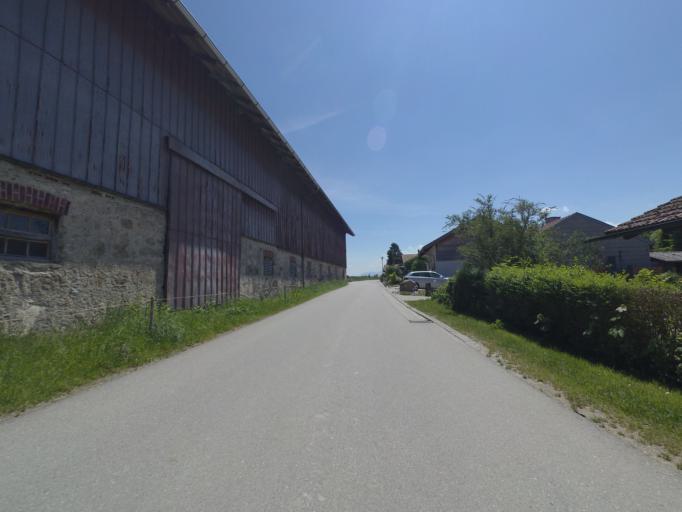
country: DE
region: Bavaria
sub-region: Upper Bavaria
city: Taching am See
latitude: 47.9540
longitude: 12.7538
